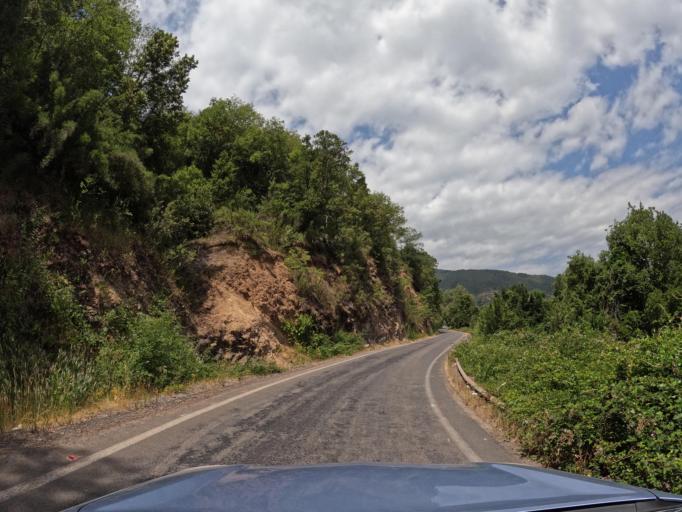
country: CL
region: Maule
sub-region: Provincia de Curico
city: Molina
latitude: -35.1816
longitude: -71.0777
